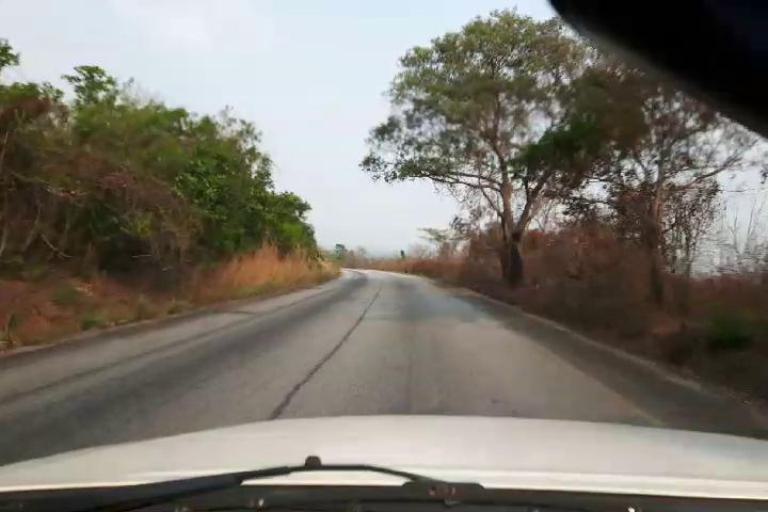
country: SL
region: Southern Province
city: Baiima
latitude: 8.1699
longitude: -11.9502
